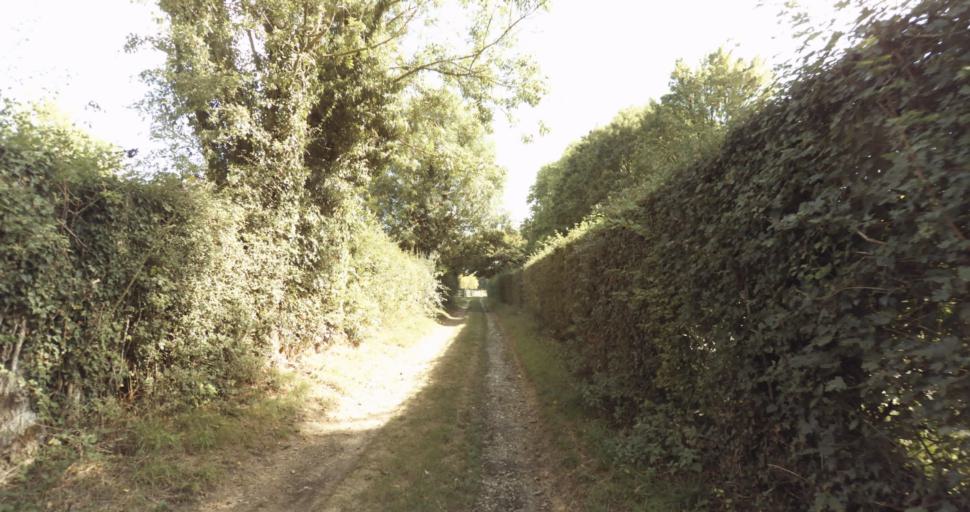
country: FR
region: Lower Normandy
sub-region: Departement de l'Orne
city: Vimoutiers
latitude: 48.9231
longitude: 0.2387
